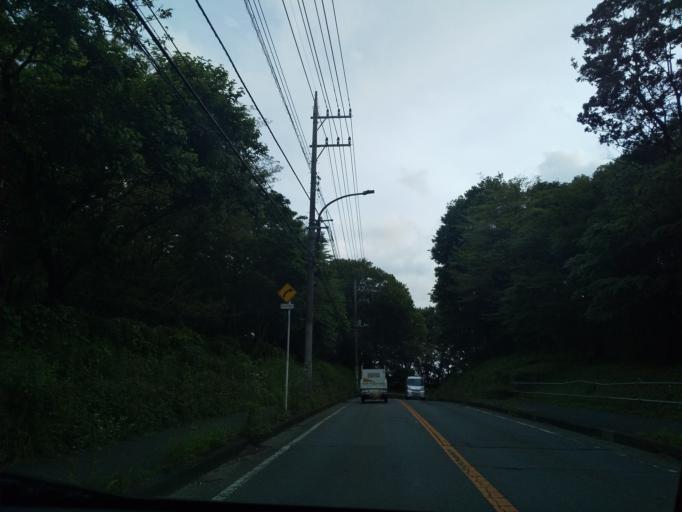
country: JP
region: Kanagawa
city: Zama
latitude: 35.5164
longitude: 139.3930
